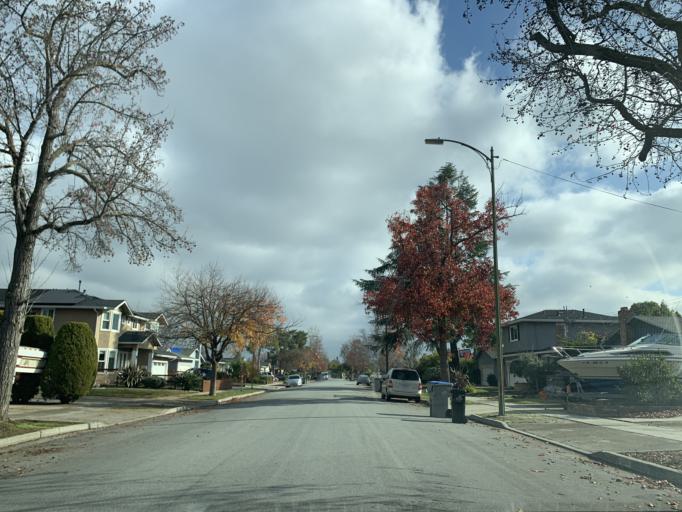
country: US
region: California
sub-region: Santa Clara County
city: Cambrian Park
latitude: 37.2548
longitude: -121.9187
